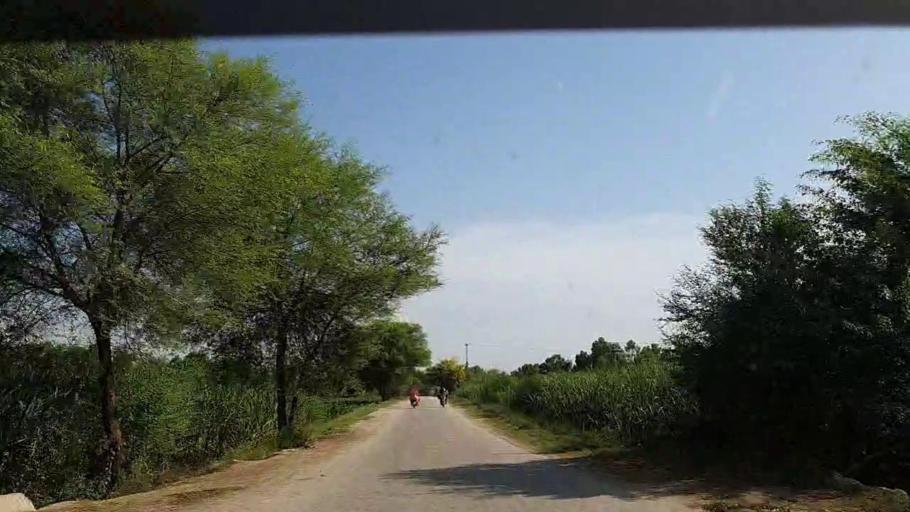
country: PK
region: Sindh
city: Adilpur
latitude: 27.9329
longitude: 69.2546
